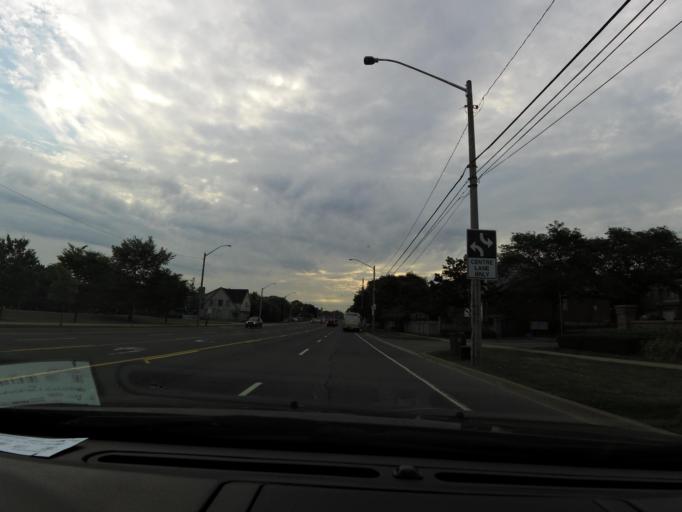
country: CA
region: Ontario
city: Hamilton
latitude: 43.2204
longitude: -79.7746
